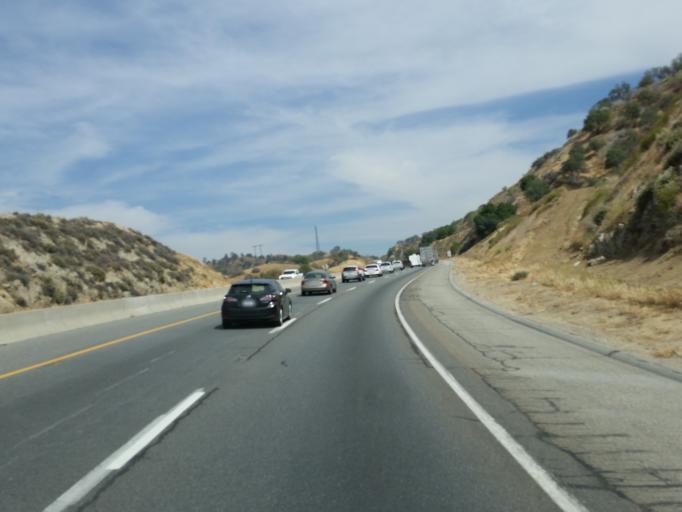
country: US
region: California
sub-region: Kern County
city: Bear Valley Springs
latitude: 35.2619
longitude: -118.6207
